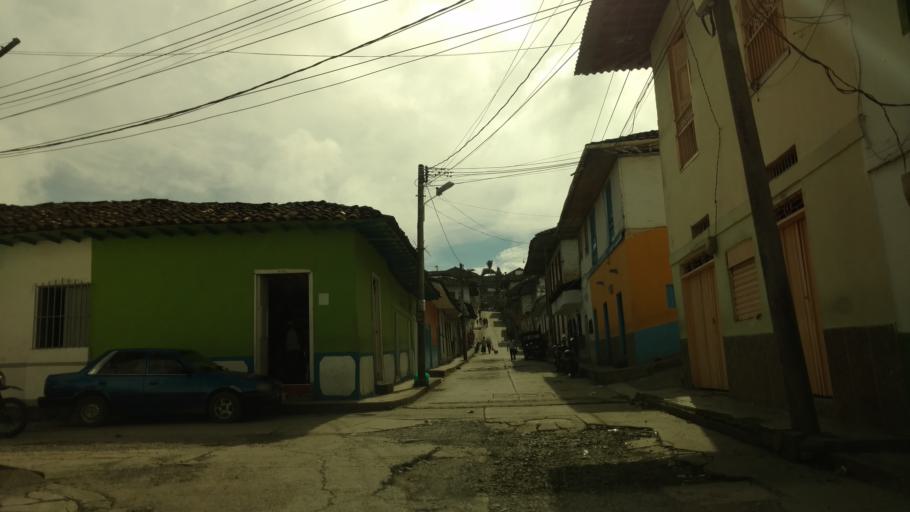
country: CO
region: Caldas
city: Aguadas
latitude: 5.6156
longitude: -75.4571
